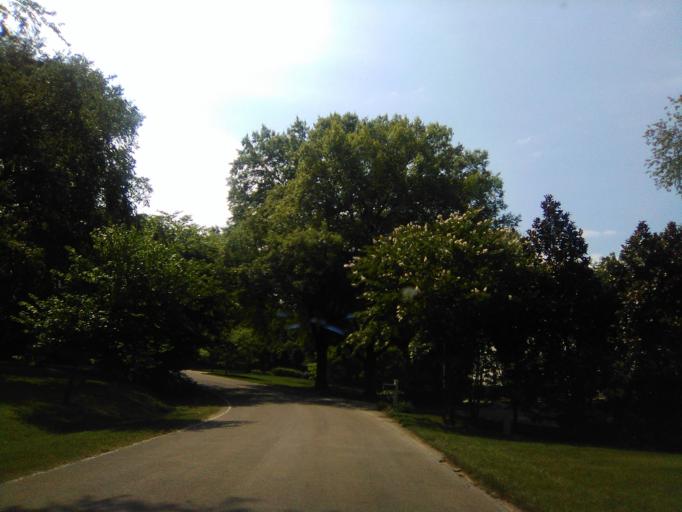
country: US
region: Tennessee
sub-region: Davidson County
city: Belle Meade
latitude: 36.1169
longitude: -86.8509
